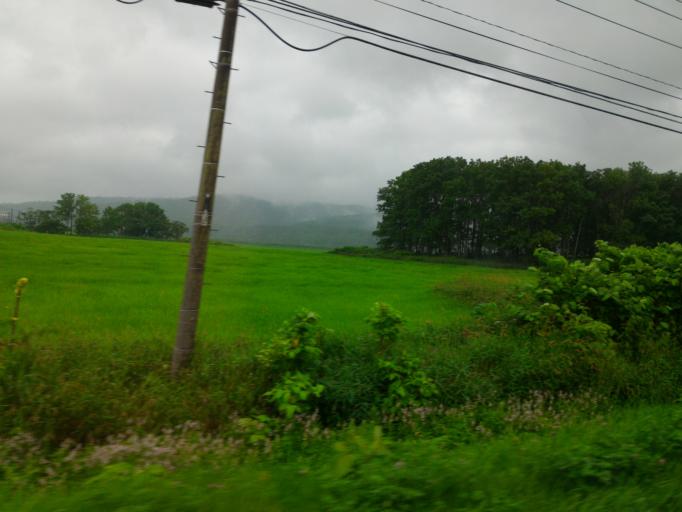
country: JP
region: Hokkaido
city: Makubetsu
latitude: 44.8706
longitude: 142.0413
